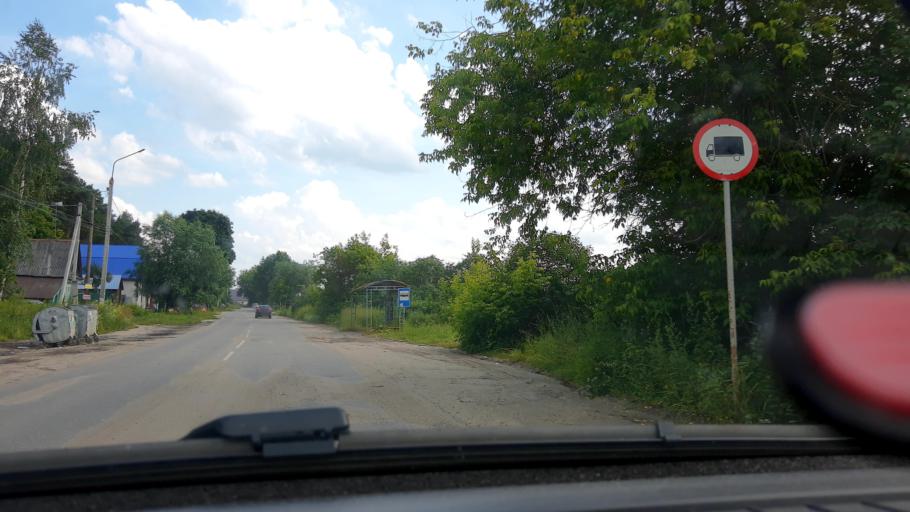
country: RU
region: Nizjnij Novgorod
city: Gorodets
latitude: 56.6669
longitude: 43.4545
